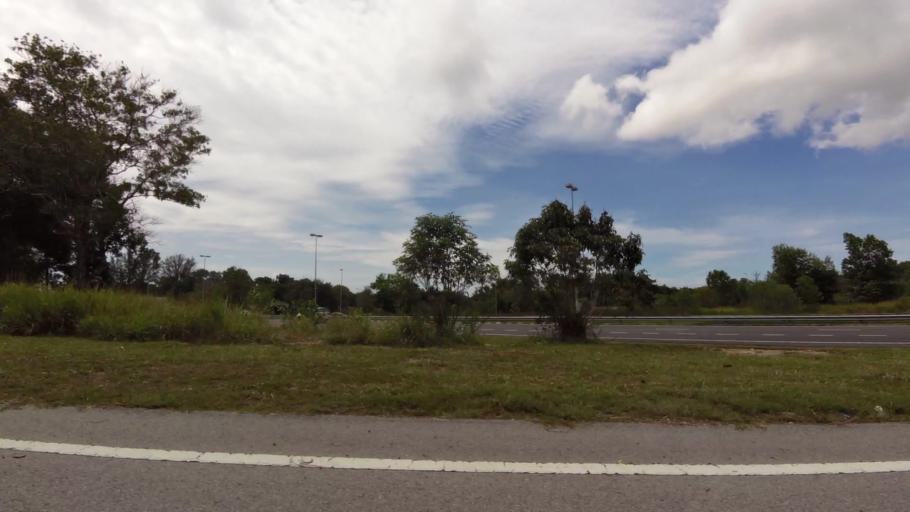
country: BN
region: Brunei and Muara
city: Bandar Seri Begawan
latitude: 4.9664
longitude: 114.8865
